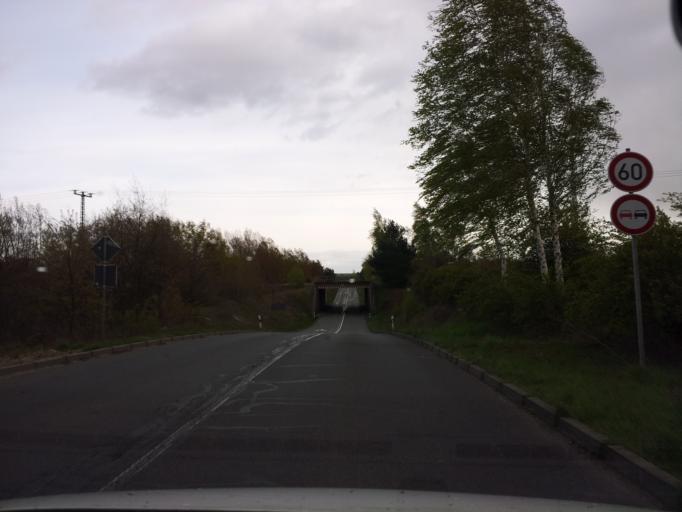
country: DE
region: Brandenburg
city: Heinersbruck
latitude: 51.7992
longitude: 14.4827
